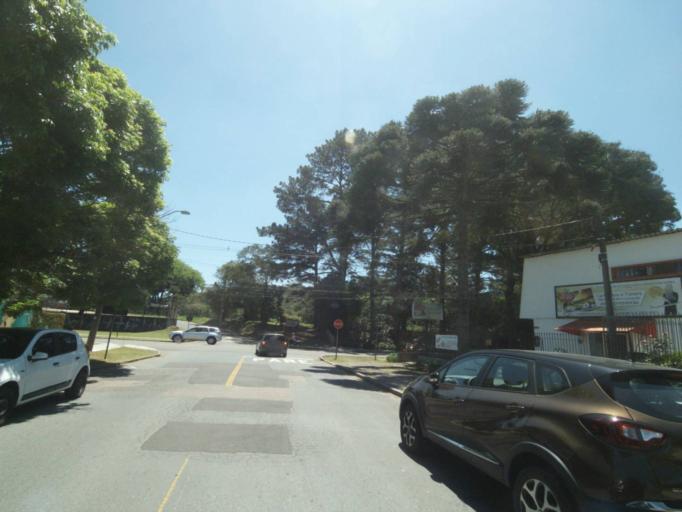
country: BR
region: Parana
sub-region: Curitiba
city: Curitiba
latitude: -25.3920
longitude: -49.2271
